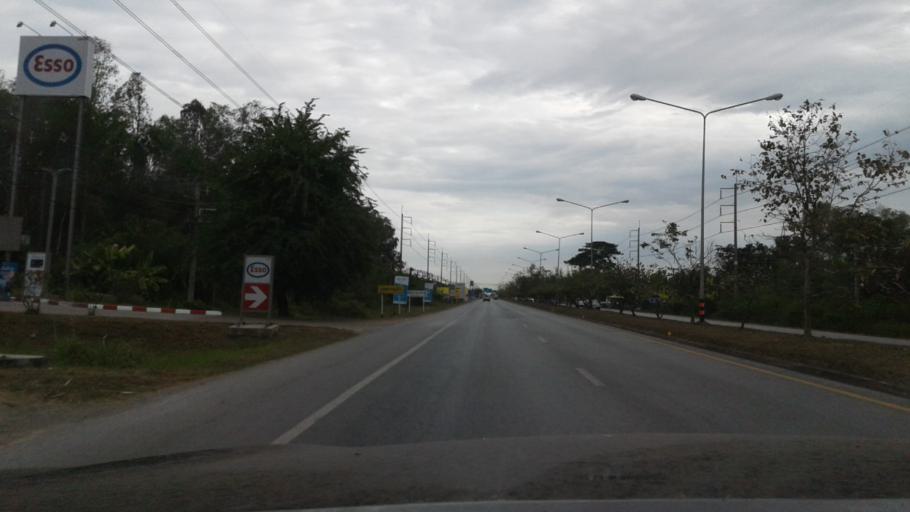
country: TH
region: Changwat Udon Thani
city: Udon Thani
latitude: 17.3674
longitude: 102.7122
